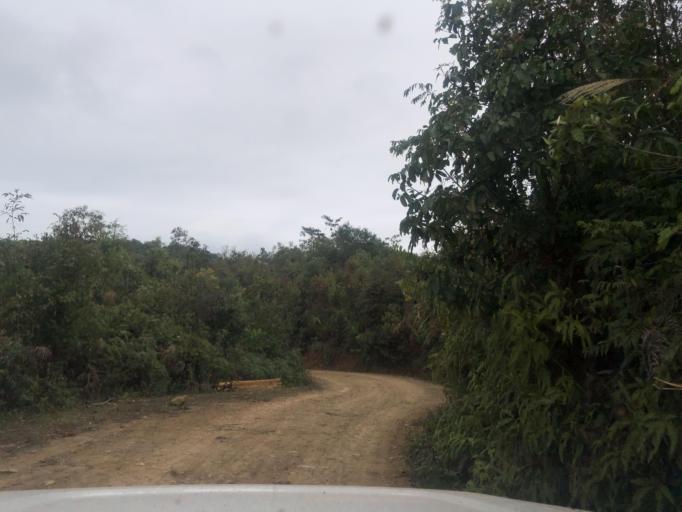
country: LA
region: Phongsali
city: Khoa
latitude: 21.2593
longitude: 102.5896
